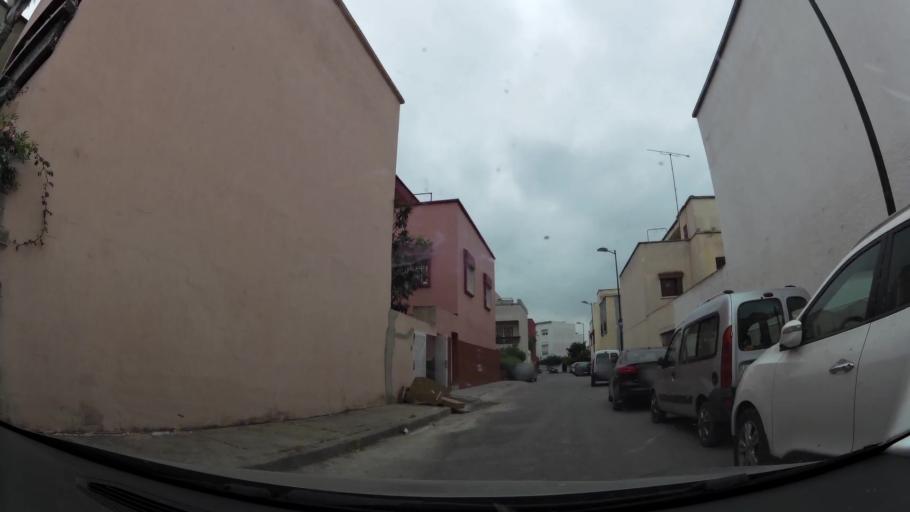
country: MA
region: Rabat-Sale-Zemmour-Zaer
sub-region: Rabat
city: Rabat
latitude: 33.9765
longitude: -6.8166
